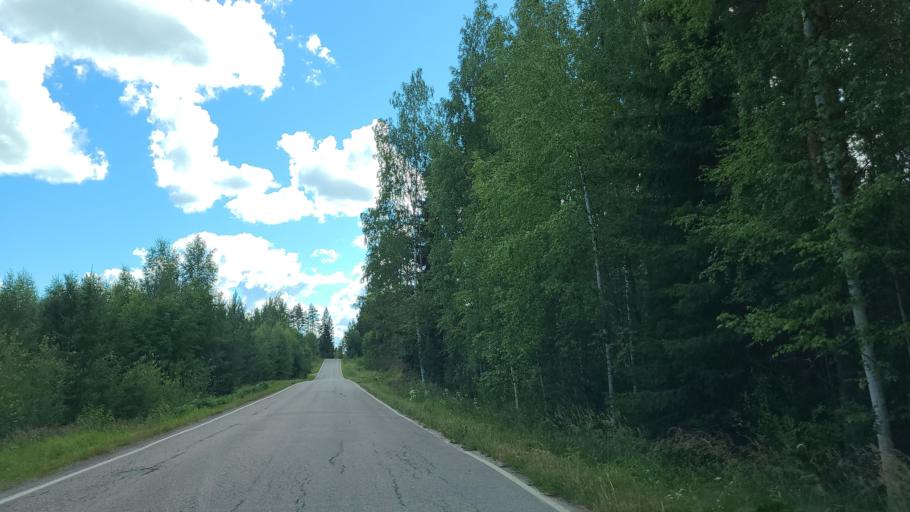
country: FI
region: Central Finland
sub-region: Jaemsae
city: Jaemsae
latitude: 61.8890
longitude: 25.2489
